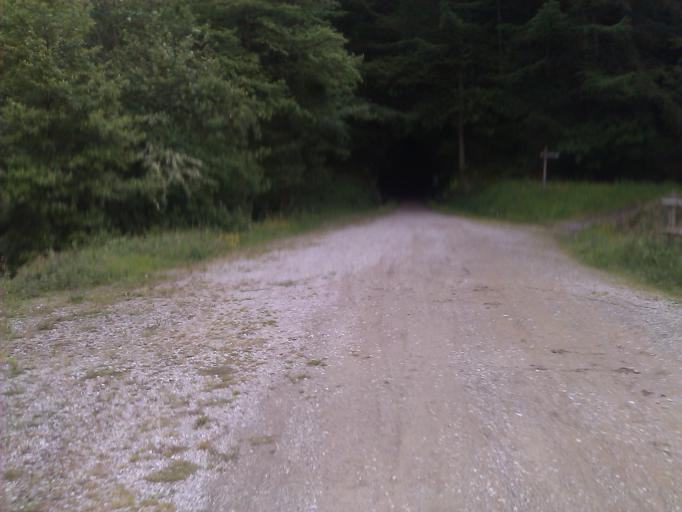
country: ES
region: Navarre
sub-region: Provincia de Navarra
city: Leitza
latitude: 43.0557
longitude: -1.9062
